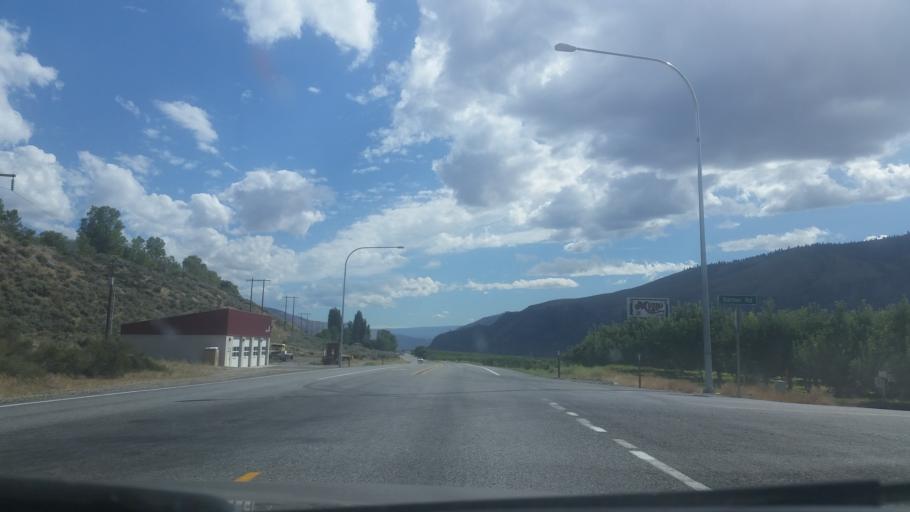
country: US
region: Washington
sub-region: Chelan County
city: Entiat
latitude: 47.7331
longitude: -120.1983
